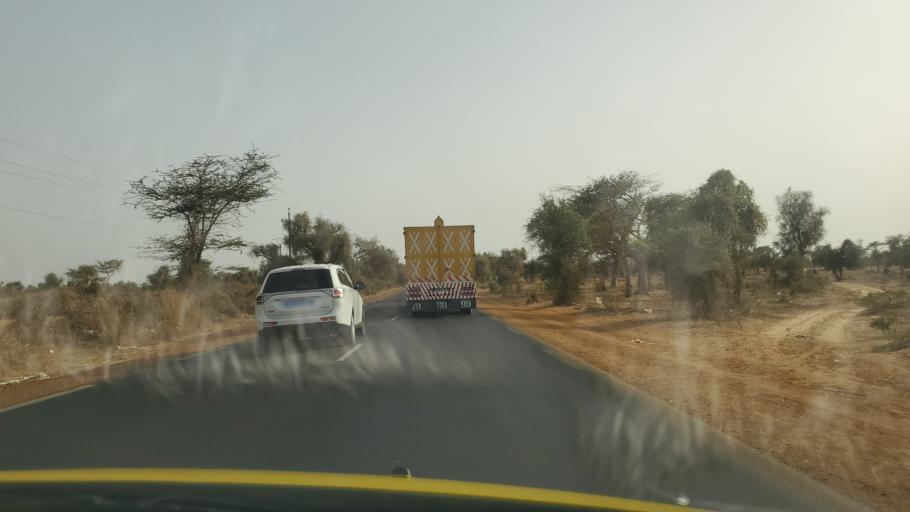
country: SN
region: Thies
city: Mekhe
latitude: 15.2716
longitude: -16.5352
